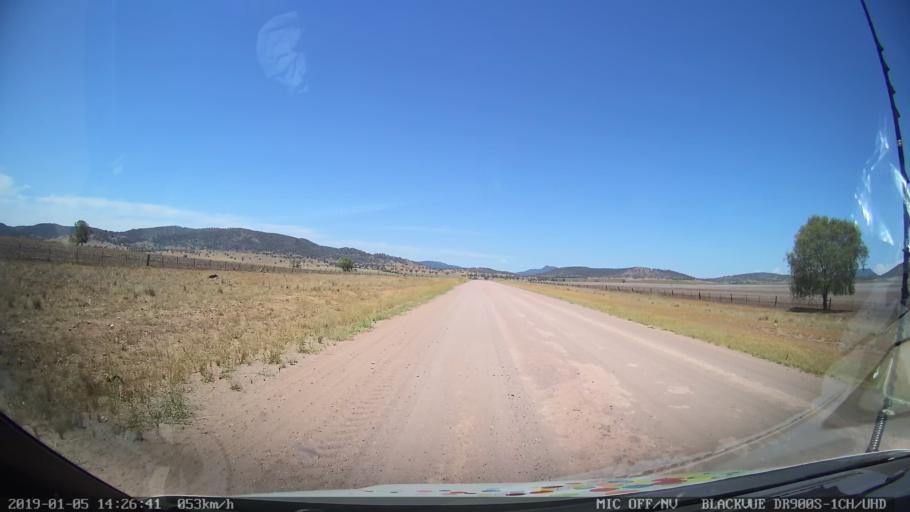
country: AU
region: New South Wales
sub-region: Liverpool Plains
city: Quirindi
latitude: -31.2372
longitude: 150.5593
